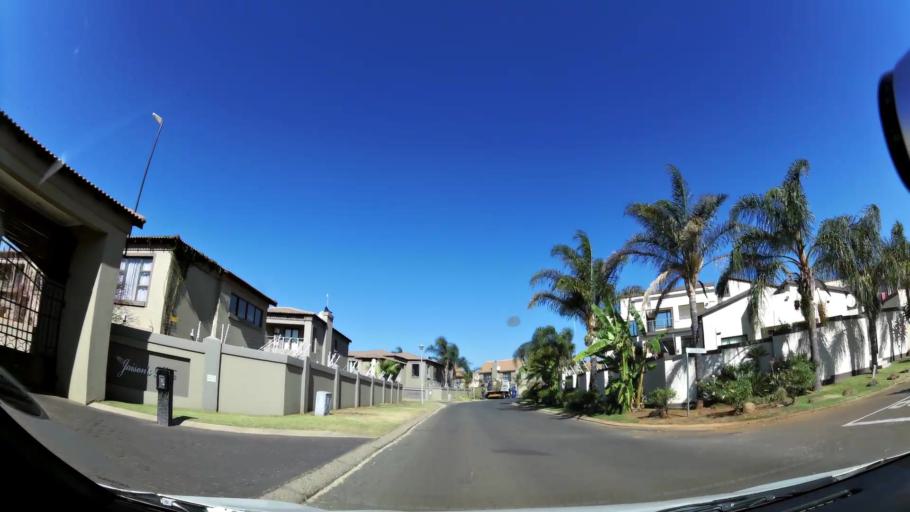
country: ZA
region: Gauteng
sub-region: Ekurhuleni Metropolitan Municipality
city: Germiston
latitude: -26.2942
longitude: 28.1030
